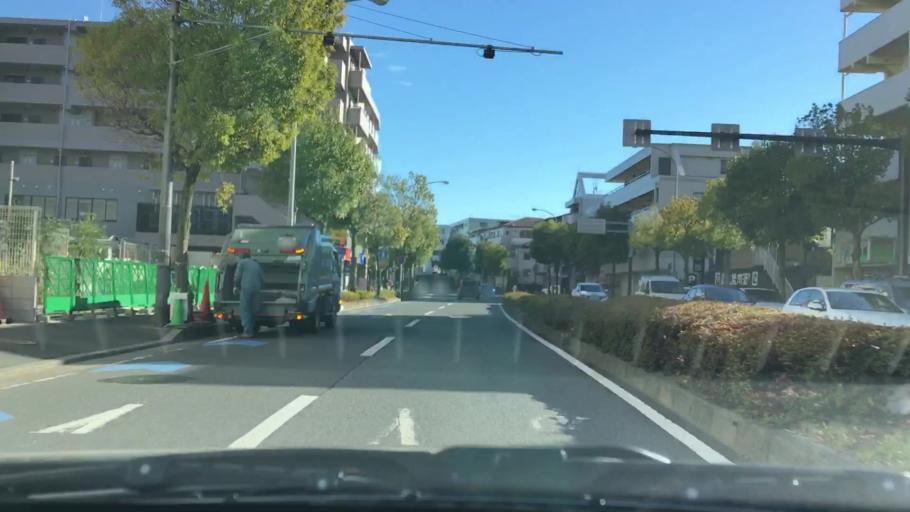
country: JP
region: Tokyo
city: Chofugaoka
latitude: 35.5429
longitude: 139.5701
